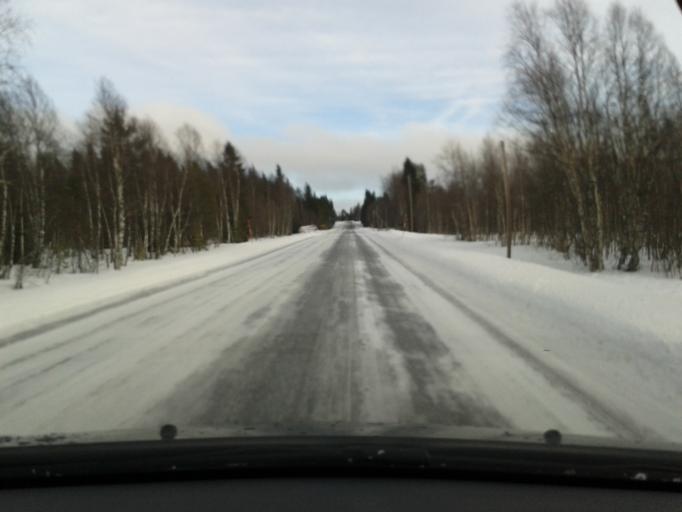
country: SE
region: Vaesterbotten
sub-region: Vilhelmina Kommun
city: Vilhelmina
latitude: 64.6339
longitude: 16.4259
